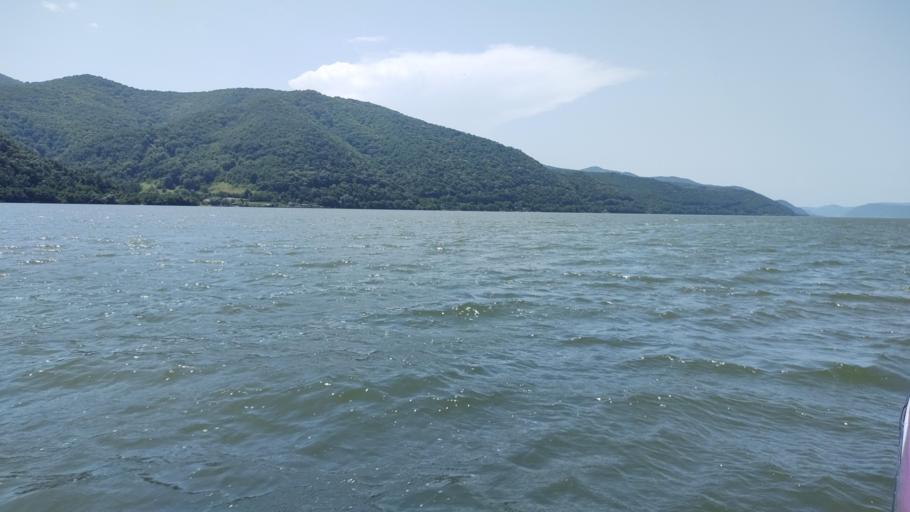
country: RO
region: Caras-Severin
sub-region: Comuna Berzasca
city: Berzasca
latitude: 44.6357
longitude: 21.9687
